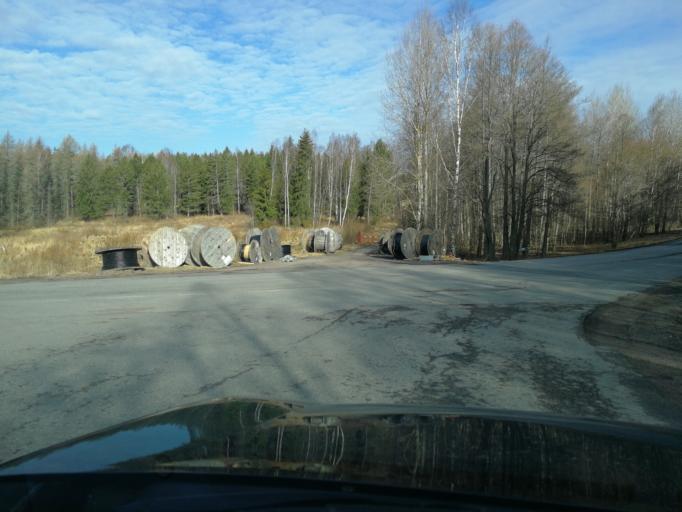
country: FI
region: Uusimaa
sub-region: Helsinki
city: Kirkkonummi
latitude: 60.0943
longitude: 24.3656
